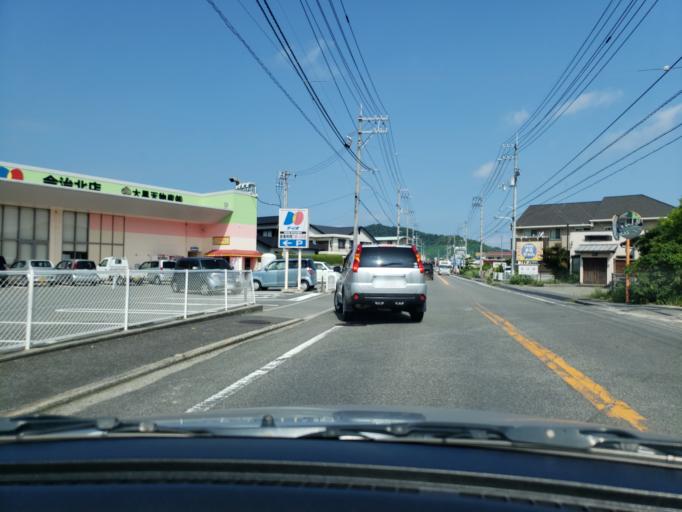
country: JP
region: Ehime
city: Hojo
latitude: 34.0986
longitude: 132.9714
